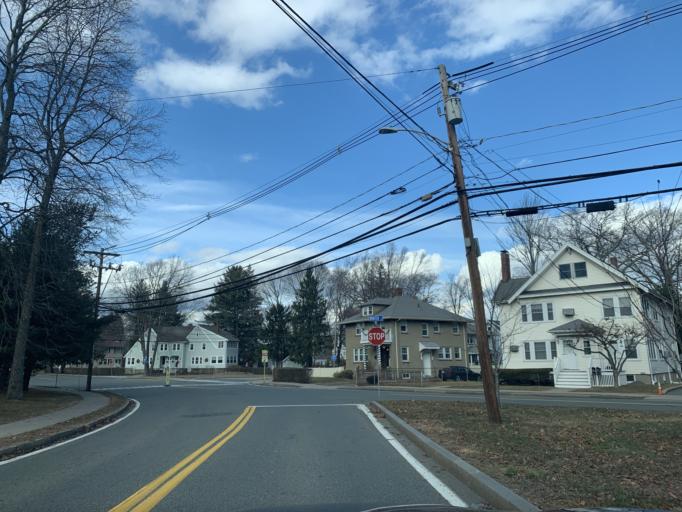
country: US
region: Massachusetts
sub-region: Norfolk County
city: Norwood
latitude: 42.1939
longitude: -71.2125
